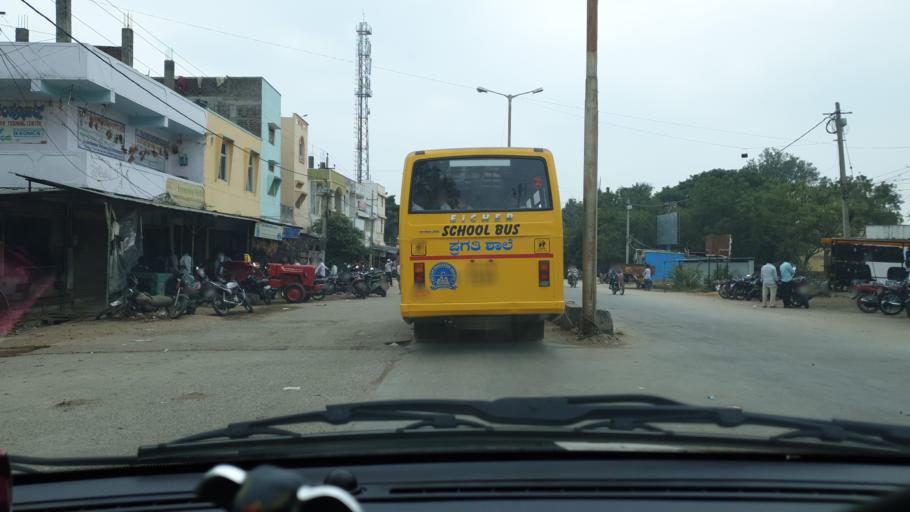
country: IN
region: Karnataka
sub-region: Yadgir
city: Gurmatkal
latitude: 16.8738
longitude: 77.3897
